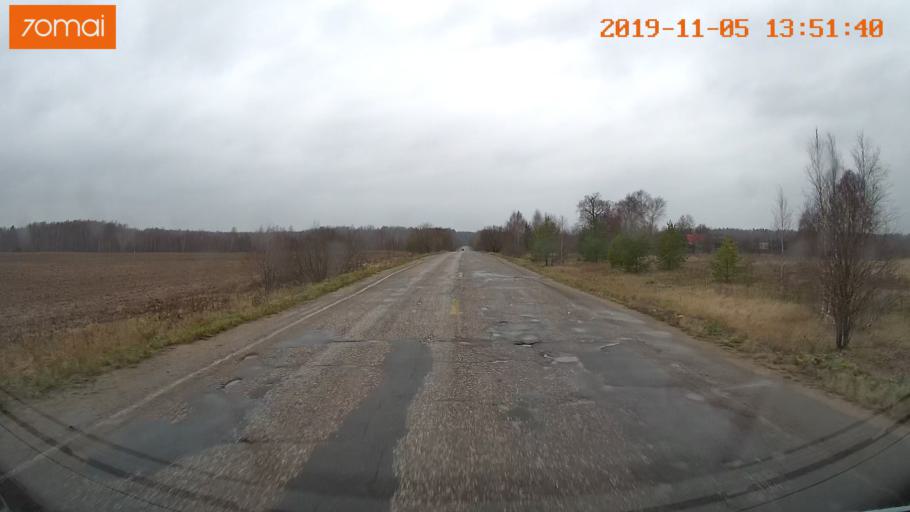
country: RU
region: Ivanovo
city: Kaminskiy
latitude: 57.0254
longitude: 41.3978
